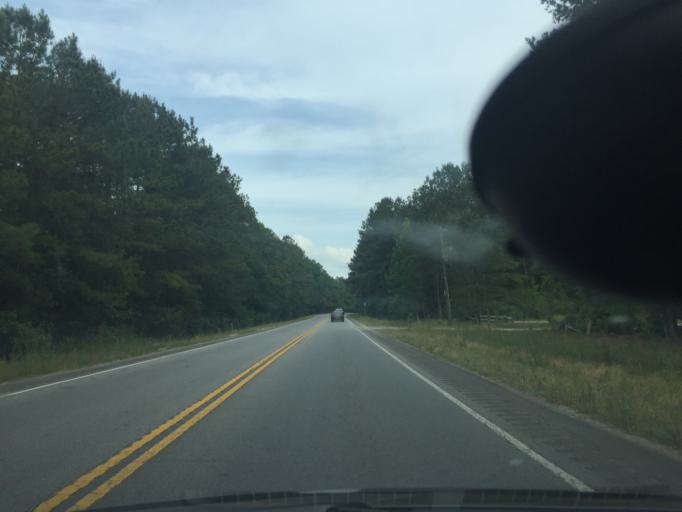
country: US
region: Georgia
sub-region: Bryan County
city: Richmond Hill
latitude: 32.0163
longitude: -81.3047
